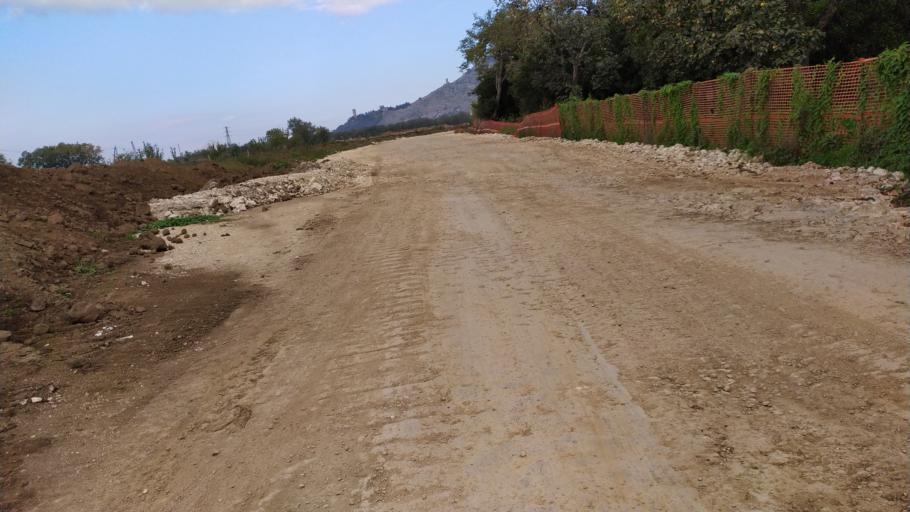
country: IT
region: Campania
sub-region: Provincia di Caserta
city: Montedecoro
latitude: 41.0199
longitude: 14.4045
